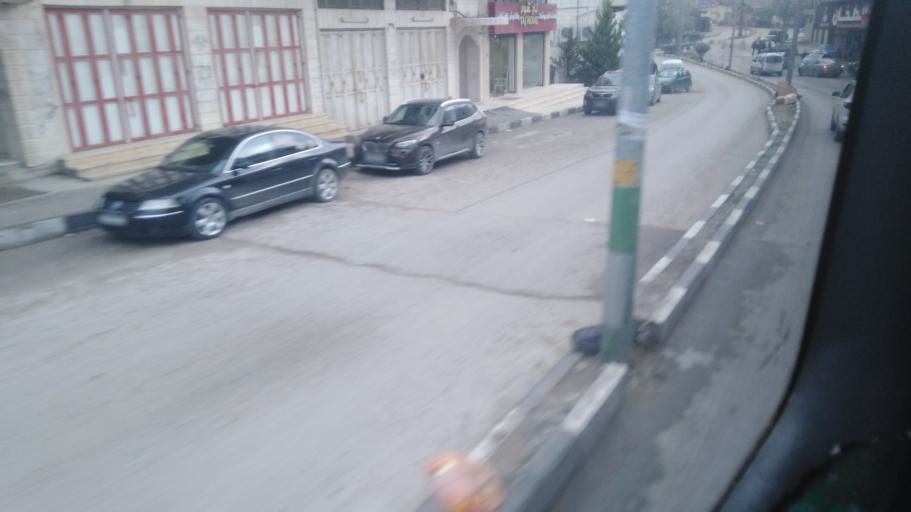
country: PS
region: West Bank
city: Hebron
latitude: 31.5285
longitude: 35.0857
